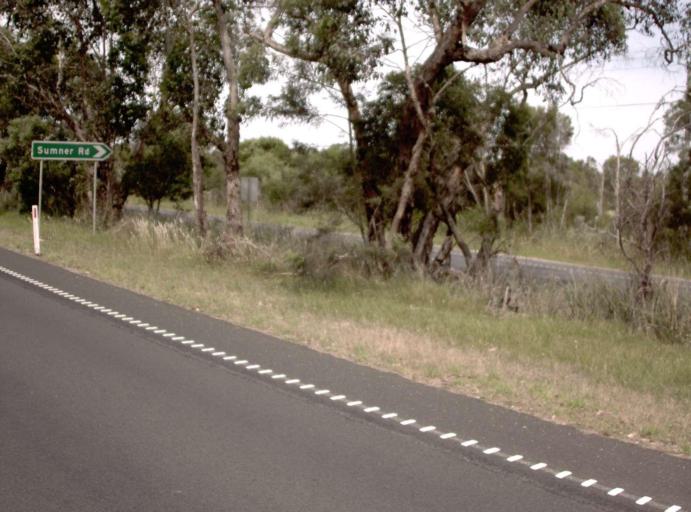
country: AU
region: Victoria
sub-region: Mornington Peninsula
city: Moorooduc
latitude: -38.2036
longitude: 145.1209
